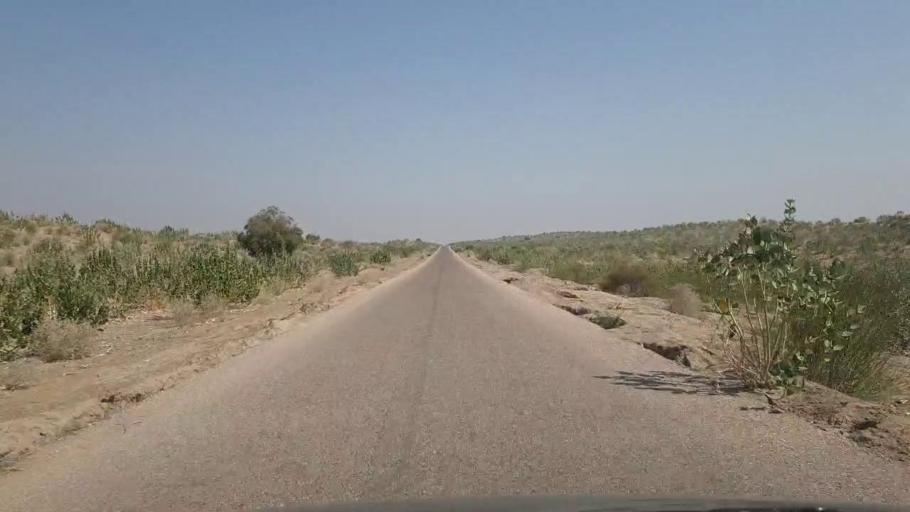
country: PK
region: Sindh
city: Chor
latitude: 25.6793
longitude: 70.1759
